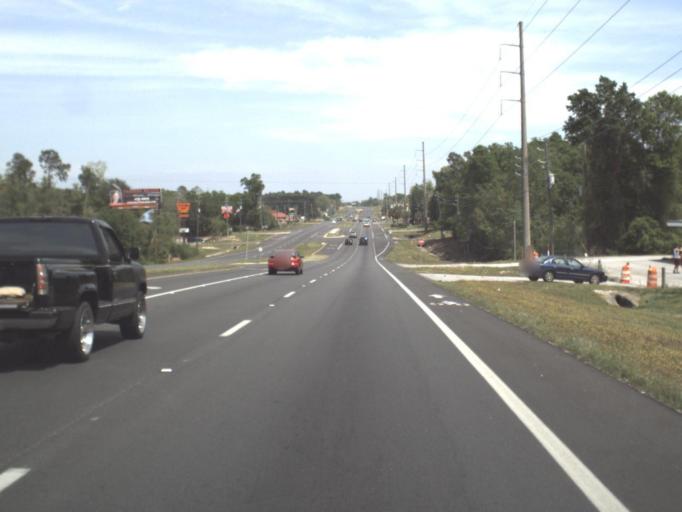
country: US
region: Florida
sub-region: Escambia County
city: Ferry Pass
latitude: 30.5324
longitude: -87.2321
